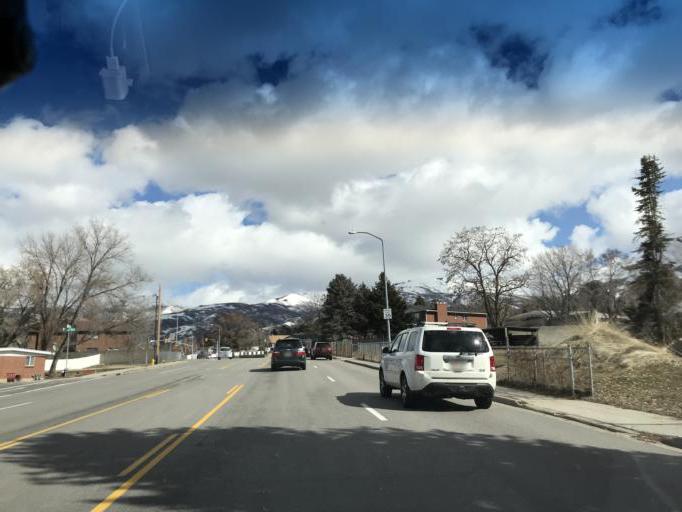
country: US
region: Utah
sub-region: Davis County
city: Woods Cross
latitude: 40.8619
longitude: -111.8832
